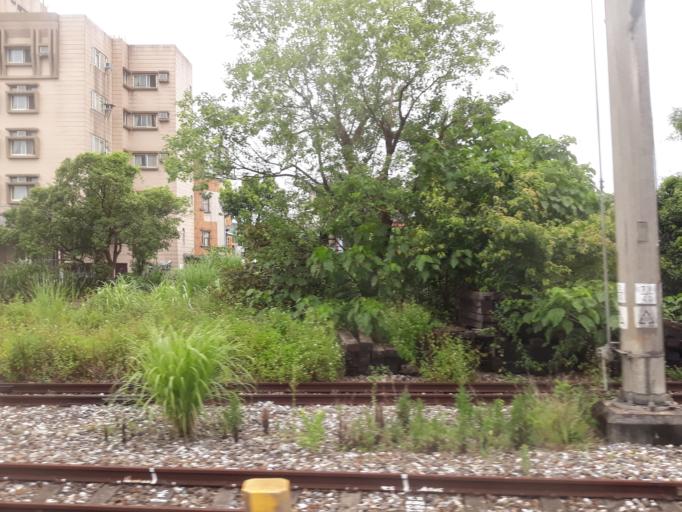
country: TW
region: Taiwan
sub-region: Yilan
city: Yilan
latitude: 24.6802
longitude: 121.7746
